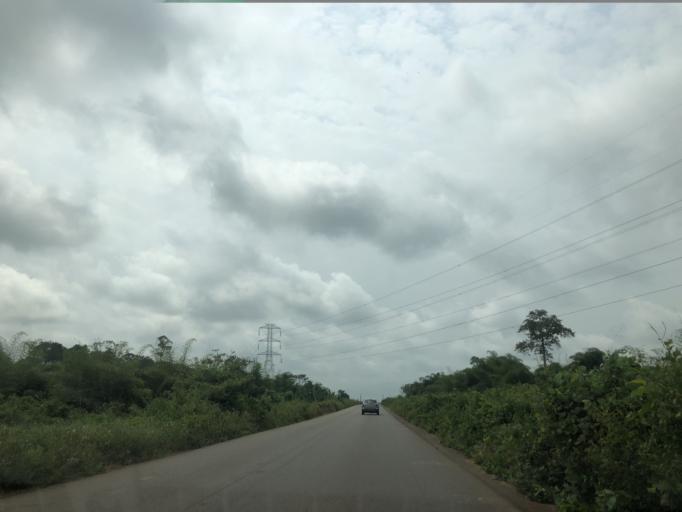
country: CM
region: Littoral
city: Edea
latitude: 3.7387
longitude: 10.1171
